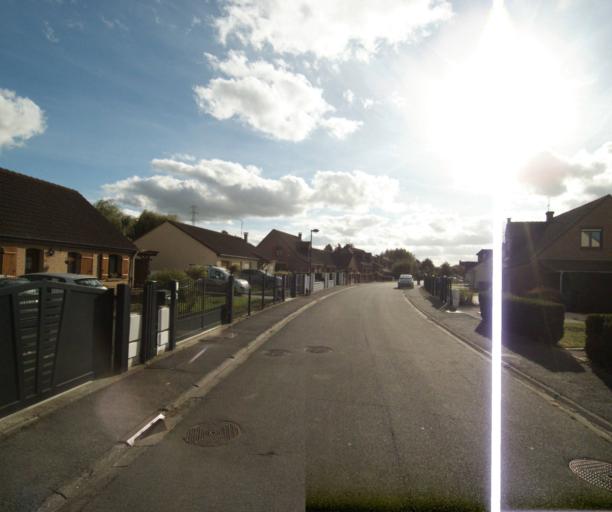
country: FR
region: Nord-Pas-de-Calais
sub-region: Departement du Nord
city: Houplines
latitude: 50.6664
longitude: 2.9072
